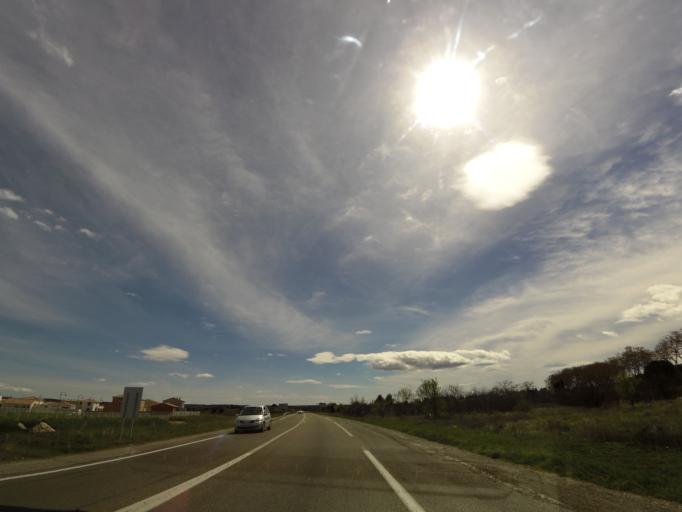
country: FR
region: Languedoc-Roussillon
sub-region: Departement du Gard
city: Bernis
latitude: 43.7670
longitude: 4.2784
